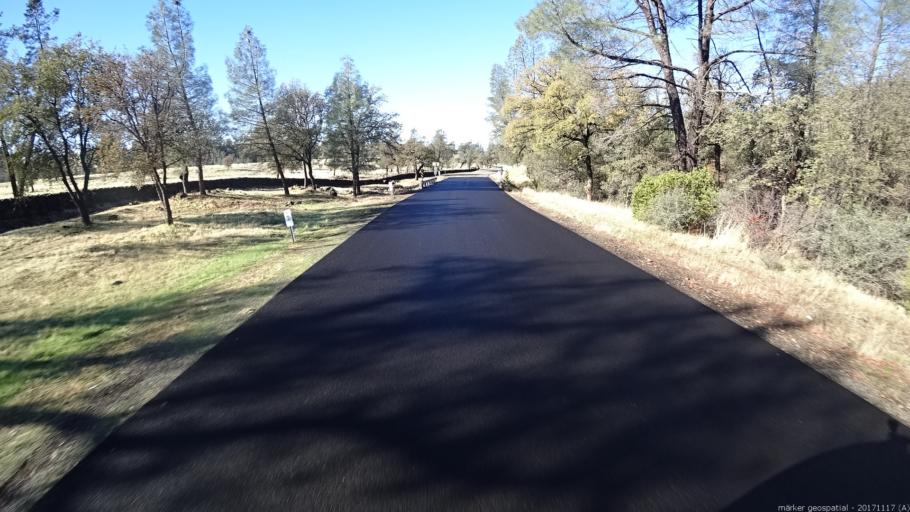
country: US
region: California
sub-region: Shasta County
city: Cottonwood
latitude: 40.4398
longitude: -122.1297
